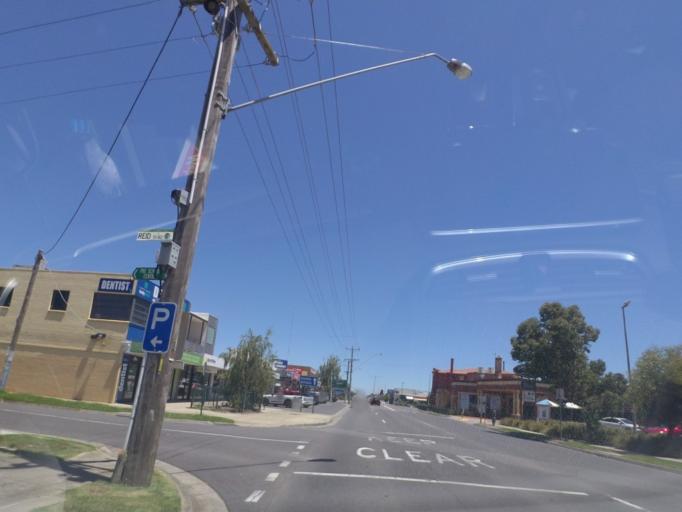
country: AU
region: Victoria
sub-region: Whittlesea
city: Mill Park
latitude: -37.6515
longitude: 145.0897
